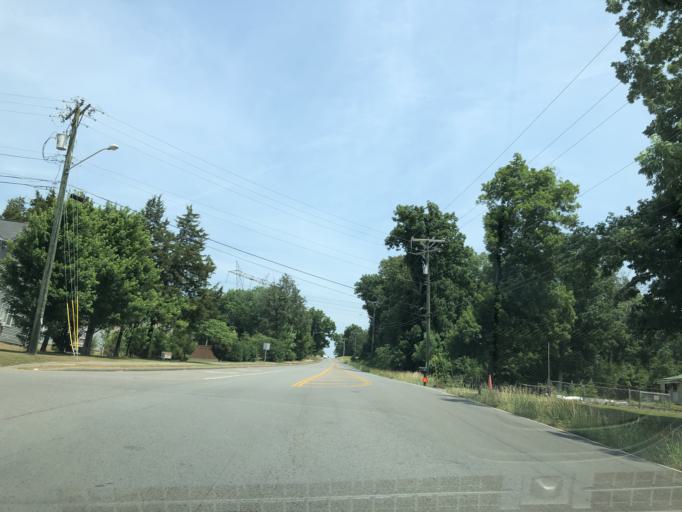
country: US
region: Tennessee
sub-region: Rutherford County
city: La Vergne
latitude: 36.0501
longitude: -86.6064
